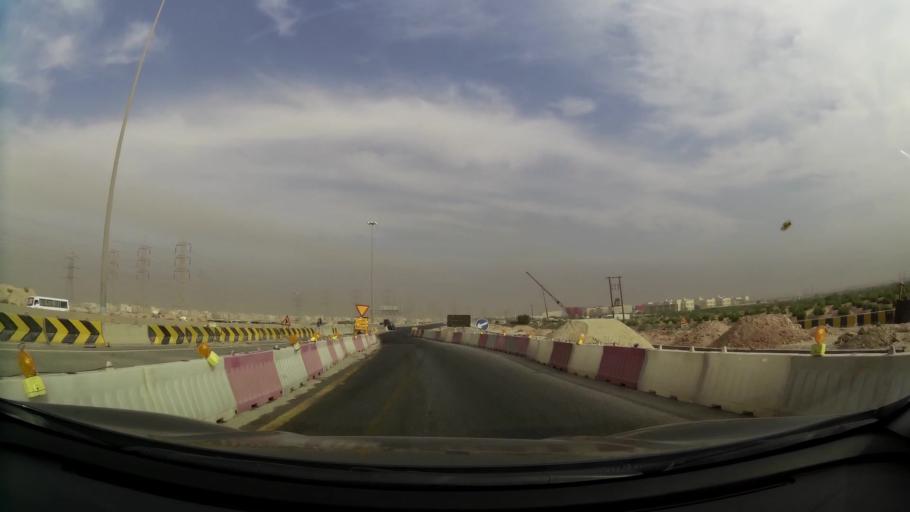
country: KW
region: Muhafazat al Jahra'
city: Al Jahra'
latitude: 29.3173
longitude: 47.7854
